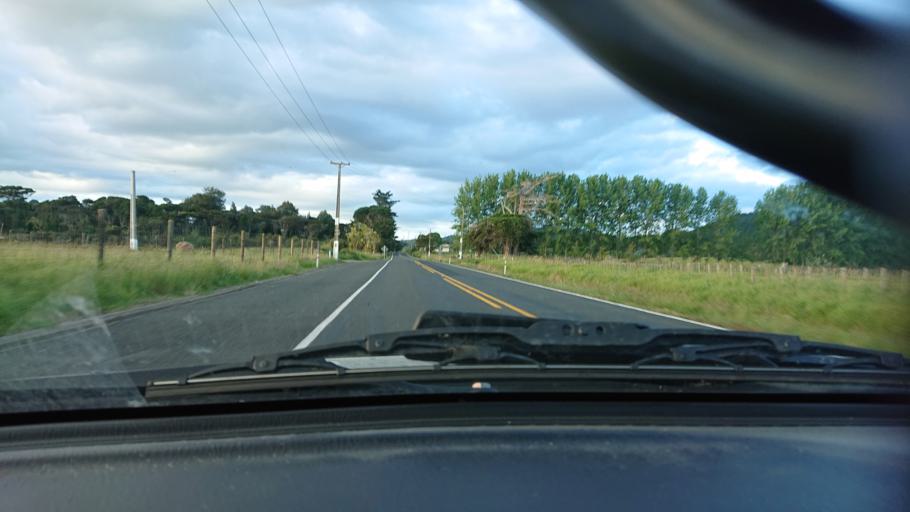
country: NZ
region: Auckland
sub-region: Auckland
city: Parakai
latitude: -36.4951
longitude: 174.4485
